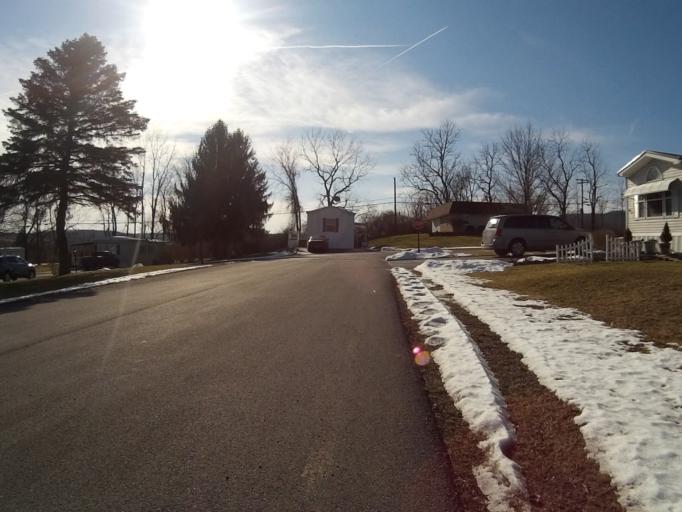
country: US
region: Pennsylvania
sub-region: Centre County
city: Houserville
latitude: 40.8699
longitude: -77.8699
